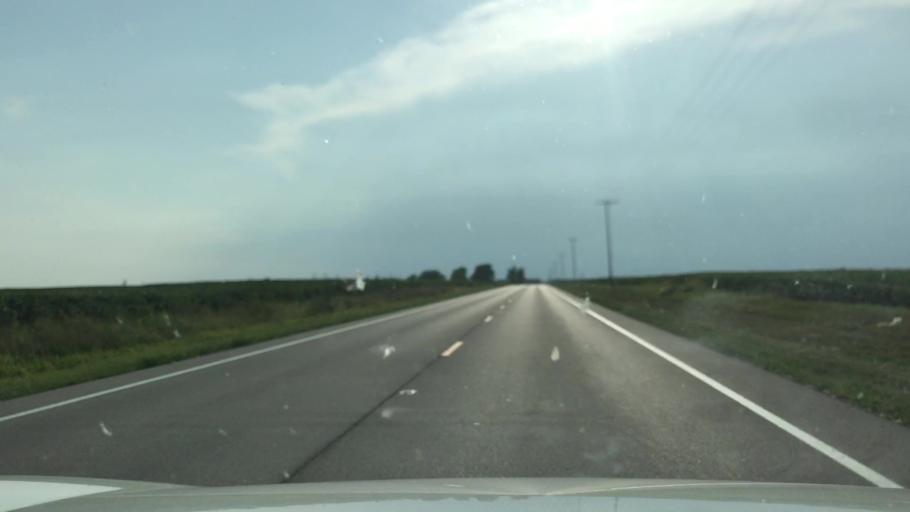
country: US
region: Illinois
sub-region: Washington County
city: Nashville
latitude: 38.4417
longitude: -89.3799
